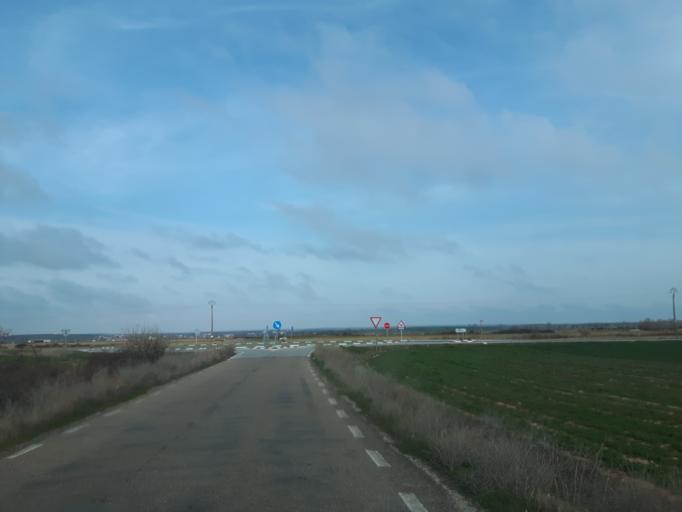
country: ES
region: Castille and Leon
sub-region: Provincia de Salamanca
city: Coca de Alba
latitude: 40.8709
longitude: -5.3768
